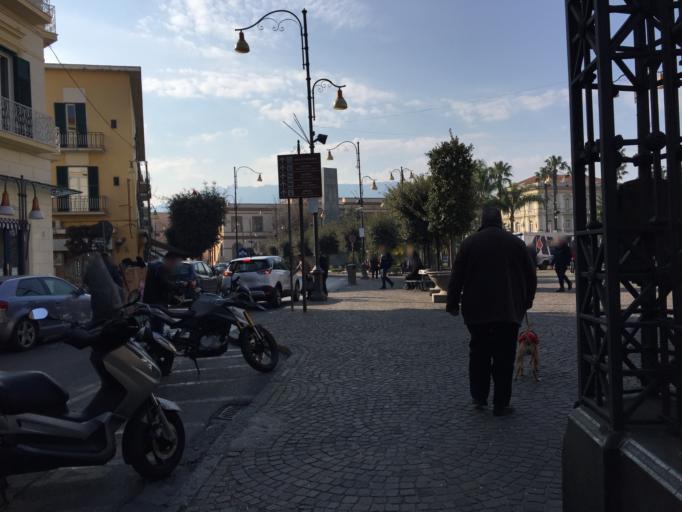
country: IT
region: Campania
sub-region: Provincia di Napoli
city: Pompei
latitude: 40.7498
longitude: 14.5012
